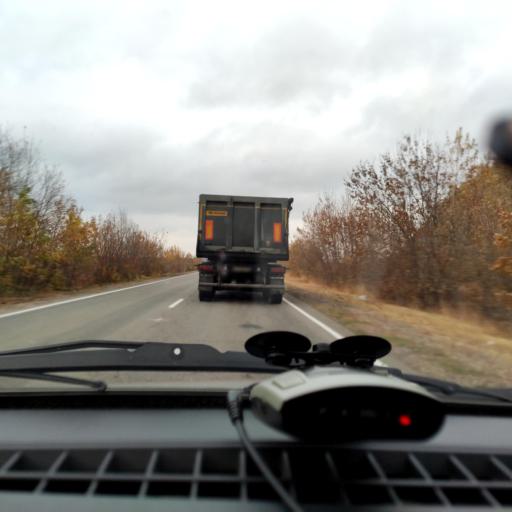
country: RU
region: Voronezj
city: Shilovo
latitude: 51.4415
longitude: 38.9964
